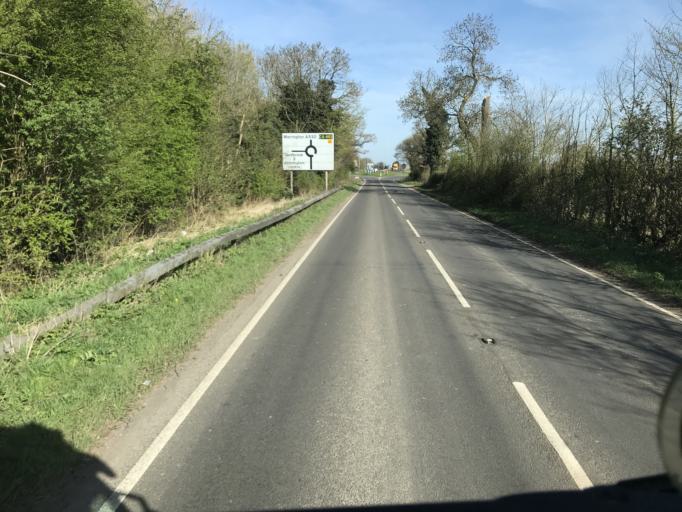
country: GB
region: England
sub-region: Cheshire West and Chester
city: Marston
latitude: 53.2445
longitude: -2.4701
